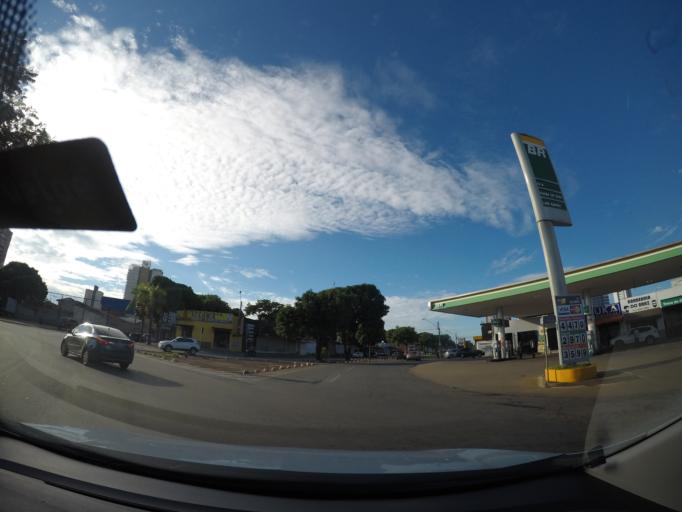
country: BR
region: Goias
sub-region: Goiania
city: Goiania
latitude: -16.7326
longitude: -49.2724
